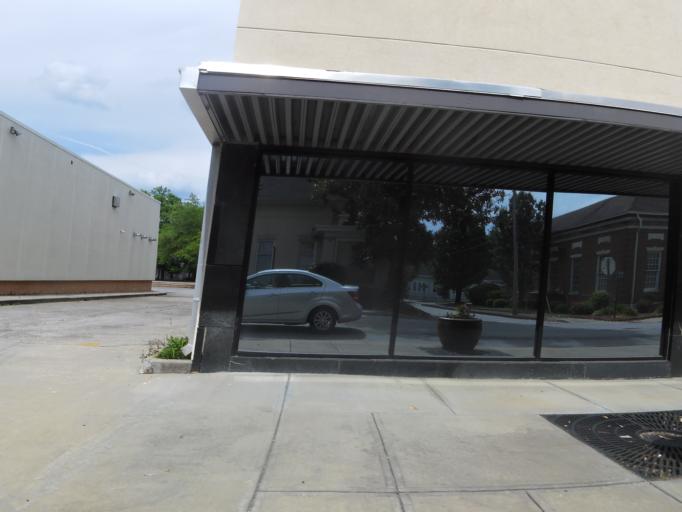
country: US
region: Georgia
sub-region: McDuffie County
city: Thomson
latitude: 33.4674
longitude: -82.5031
